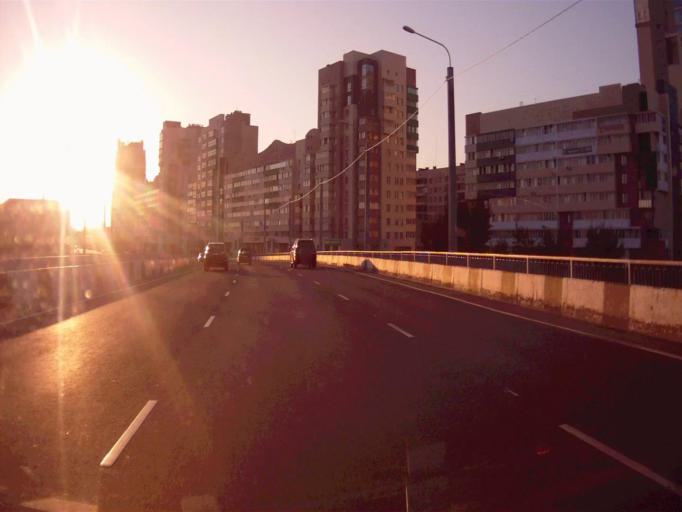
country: RU
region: Chelyabinsk
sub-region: Gorod Chelyabinsk
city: Chelyabinsk
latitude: 55.1734
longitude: 61.4067
